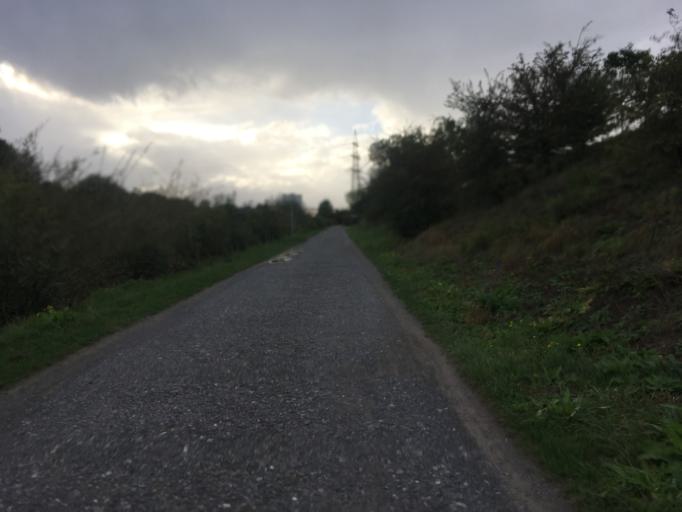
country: DE
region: North Rhine-Westphalia
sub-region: Regierungsbezirk Dusseldorf
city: Oberhausen
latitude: 51.4948
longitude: 6.9033
